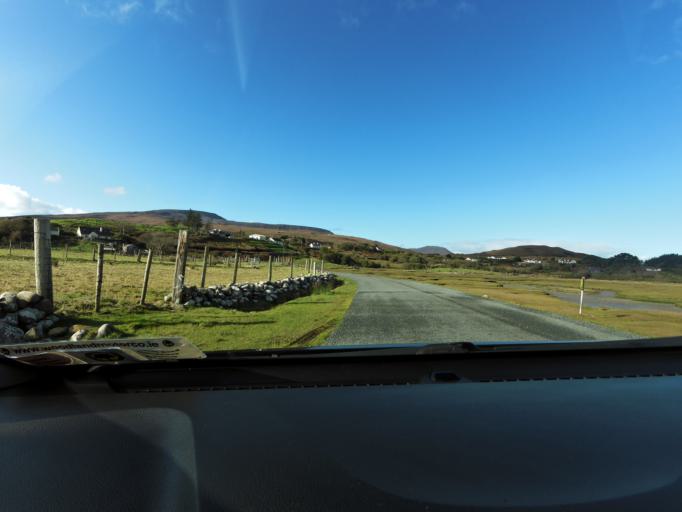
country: IE
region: Connaught
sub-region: Maigh Eo
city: Westport
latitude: 53.8982
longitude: -9.7856
